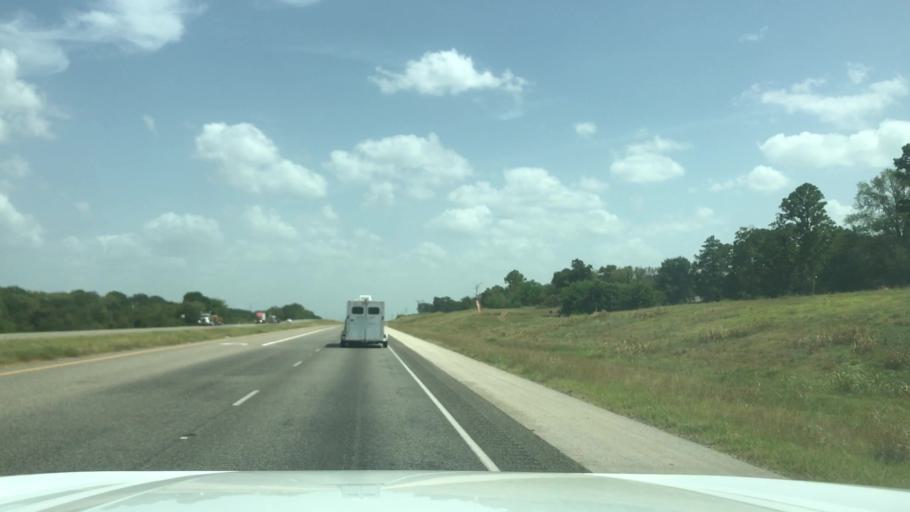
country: US
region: Texas
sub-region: Robertson County
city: Hearne
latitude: 30.9286
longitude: -96.6313
